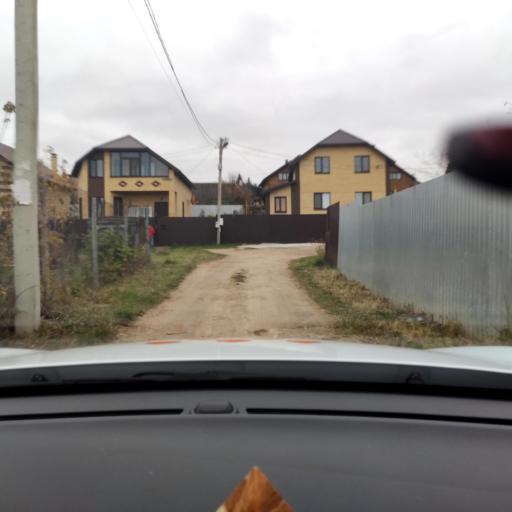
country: RU
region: Tatarstan
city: Vysokaya Gora
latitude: 55.8745
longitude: 49.2536
